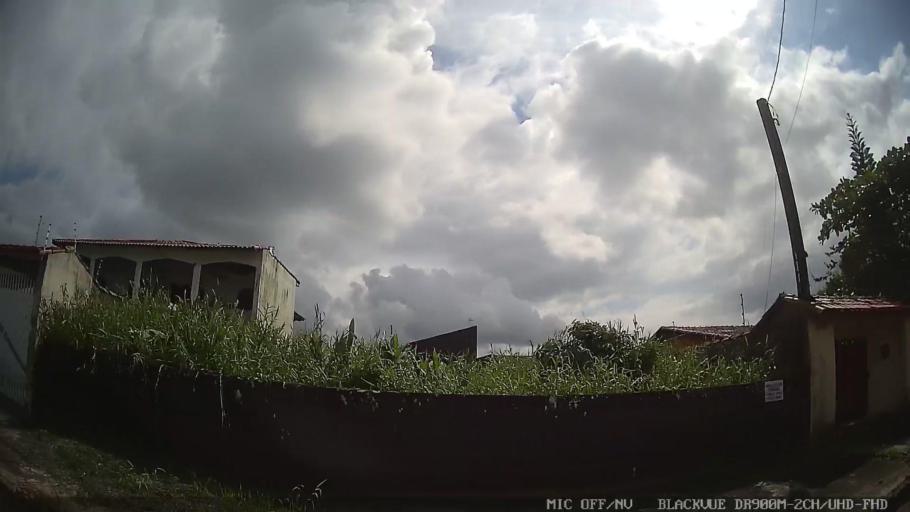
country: BR
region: Sao Paulo
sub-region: Itanhaem
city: Itanhaem
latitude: -24.2012
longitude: -46.8396
